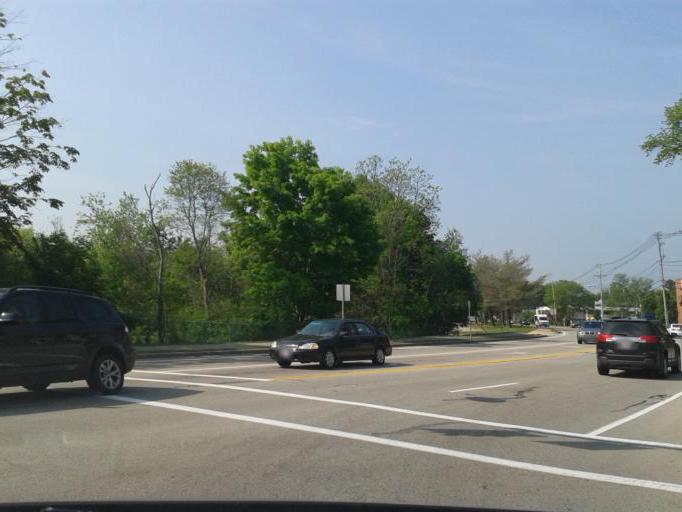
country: US
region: Massachusetts
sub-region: Worcester County
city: Westborough
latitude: 42.2794
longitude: -71.6064
